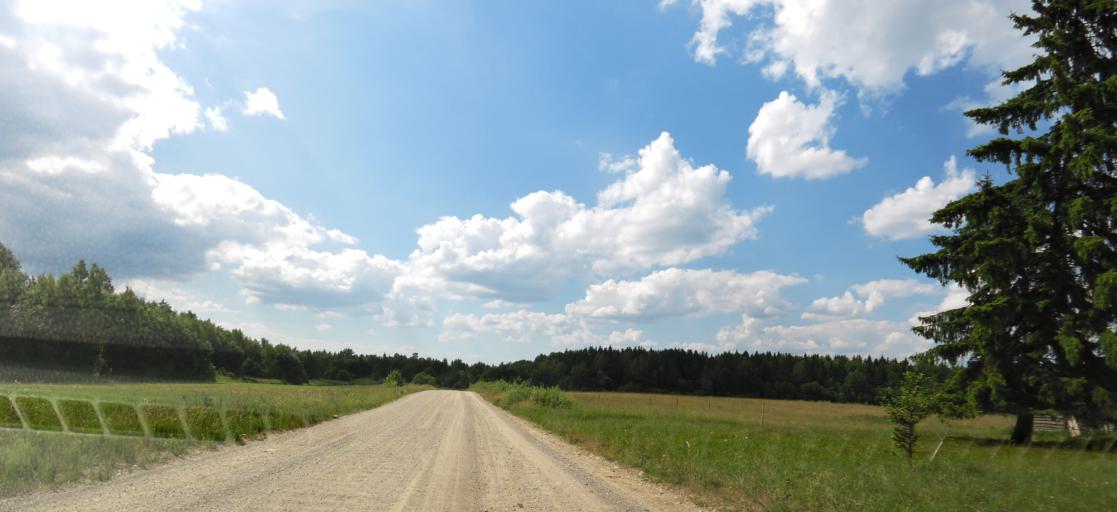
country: LT
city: Skaidiskes
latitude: 54.5306
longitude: 25.6365
